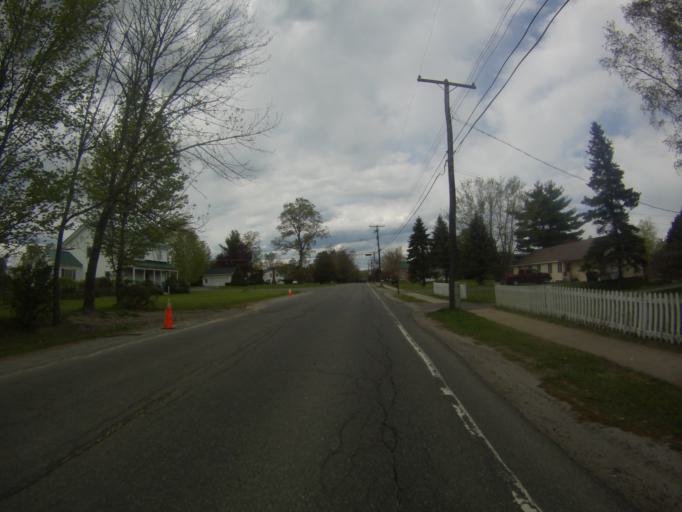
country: US
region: New York
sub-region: Essex County
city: Mineville
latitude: 44.0527
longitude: -73.5076
